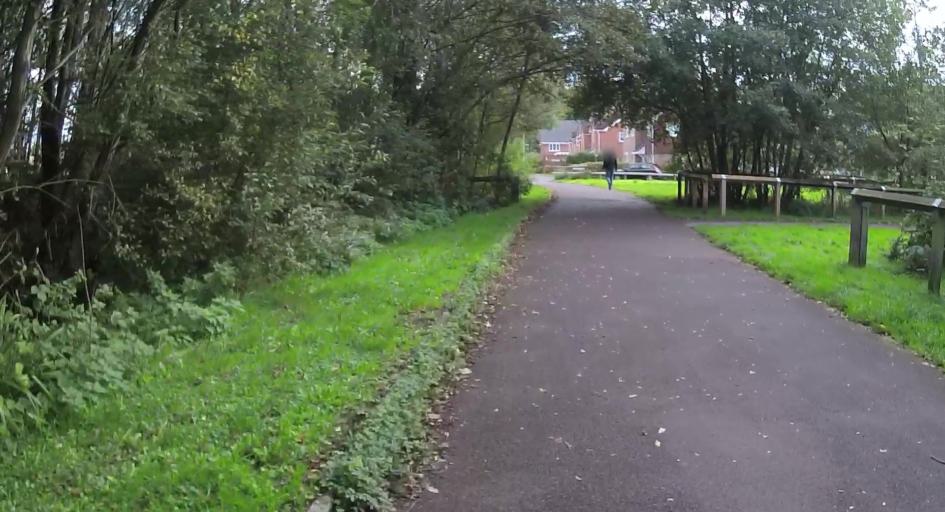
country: GB
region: England
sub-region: Hampshire
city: Fleet
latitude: 51.2941
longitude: -0.8442
